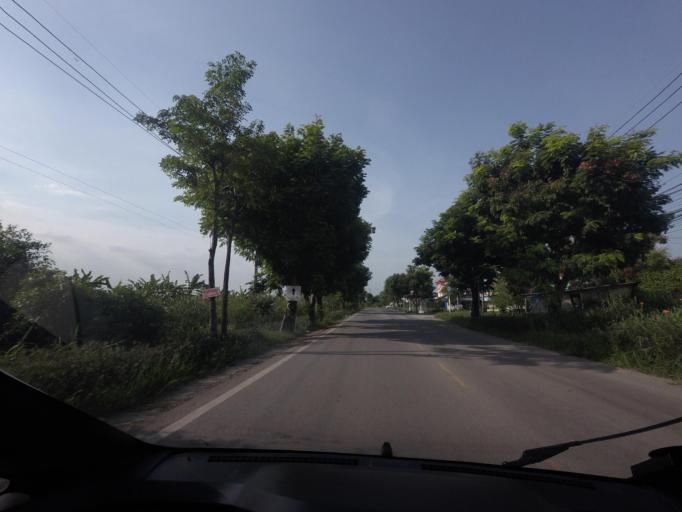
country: TH
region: Samut Prakan
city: Ban Khlong Bang Sao Thong
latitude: 13.7016
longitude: 100.8532
